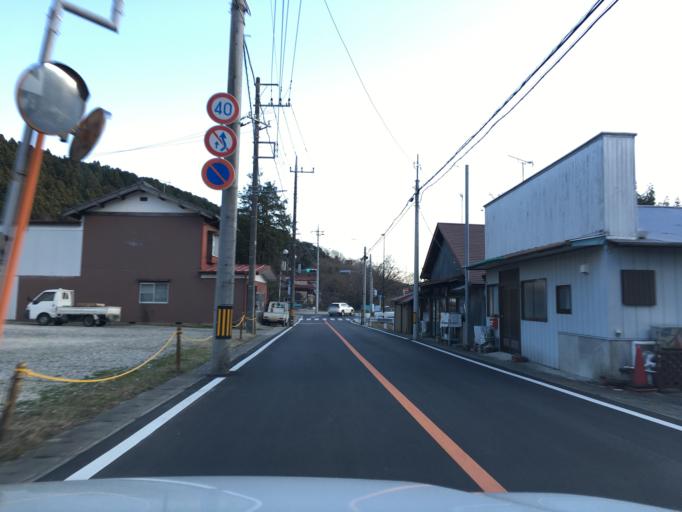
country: JP
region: Tochigi
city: Otawara
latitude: 36.8653
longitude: 140.1260
